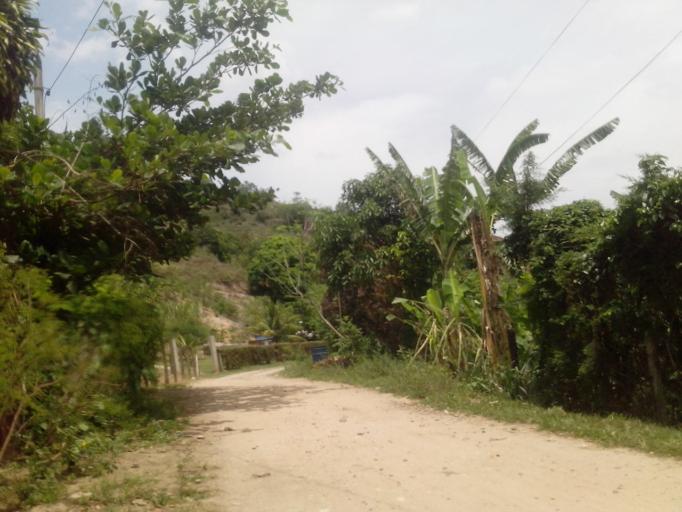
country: BR
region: Rio de Janeiro
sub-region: Miguel Pereira
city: Miguel Pereira
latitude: -22.4921
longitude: -43.4578
